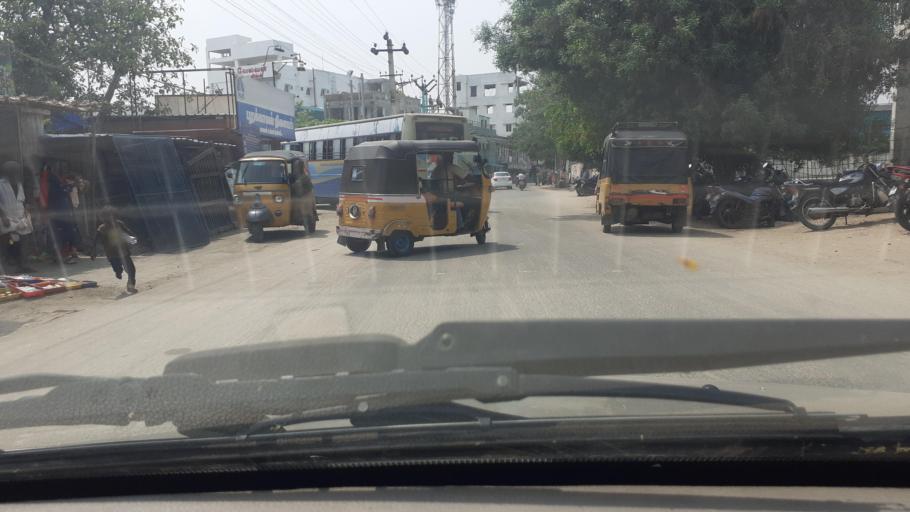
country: IN
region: Tamil Nadu
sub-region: Thoothukkudi
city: Korampallam
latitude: 8.8038
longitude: 78.1402
